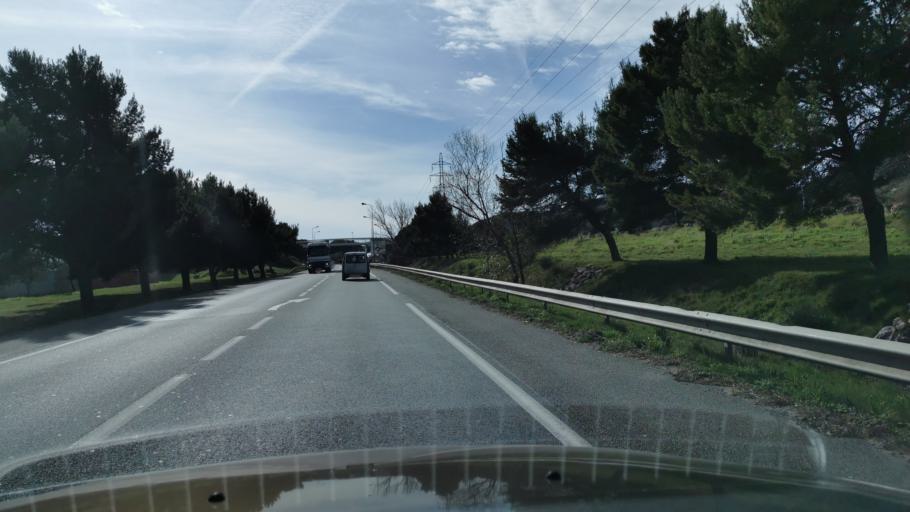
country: FR
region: Languedoc-Roussillon
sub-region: Departement de l'Aude
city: Narbonne
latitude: 43.1888
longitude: 2.9745
